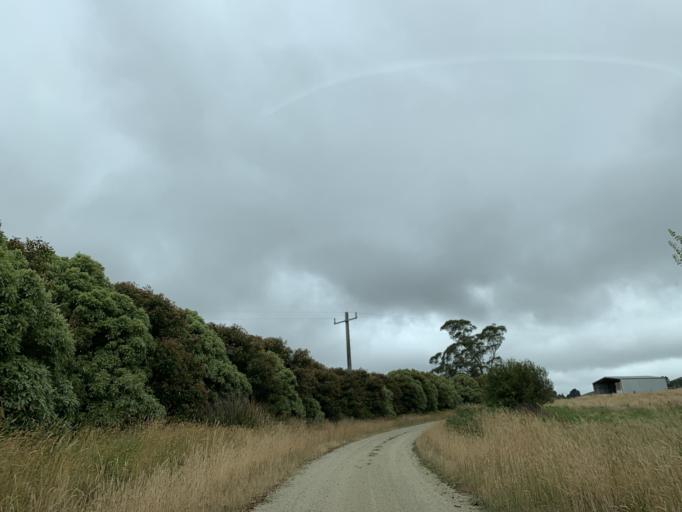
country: AU
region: Victoria
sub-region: Baw Baw
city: Warragul
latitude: -38.2953
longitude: 145.8886
